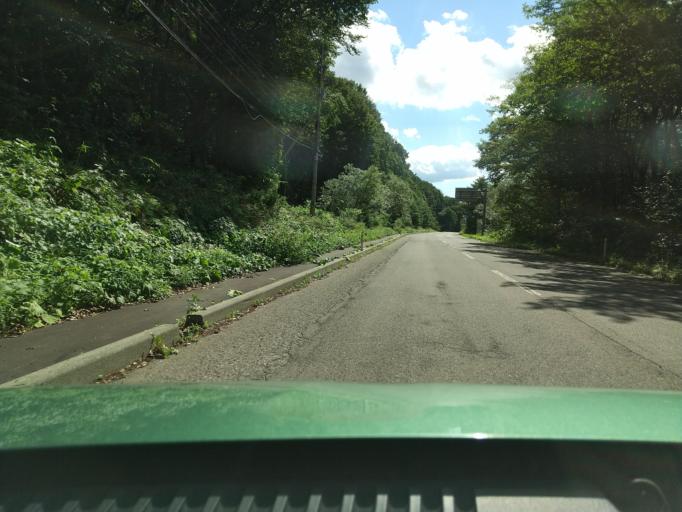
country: JP
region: Iwate
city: Shizukuishi
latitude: 39.7683
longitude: 140.7633
